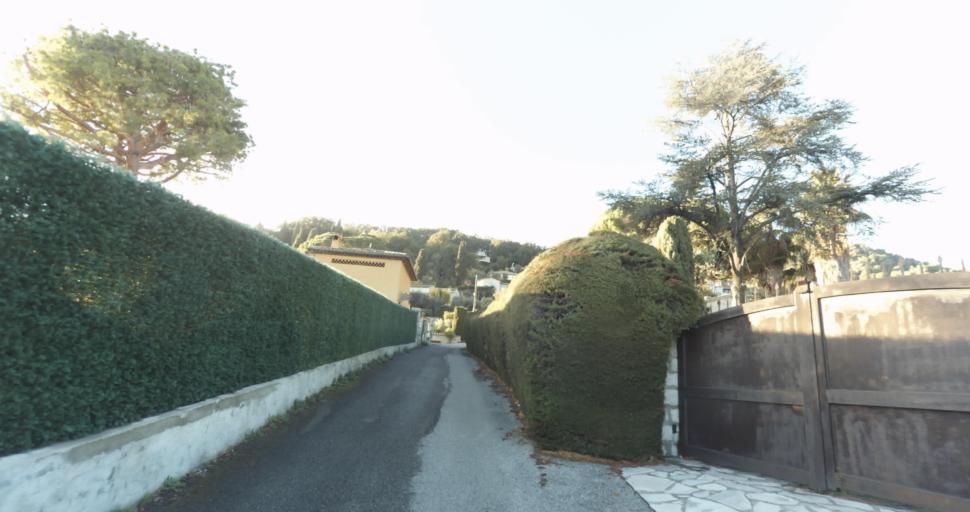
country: FR
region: Provence-Alpes-Cote d'Azur
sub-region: Departement des Alpes-Maritimes
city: Vence
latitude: 43.7293
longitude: 7.1026
